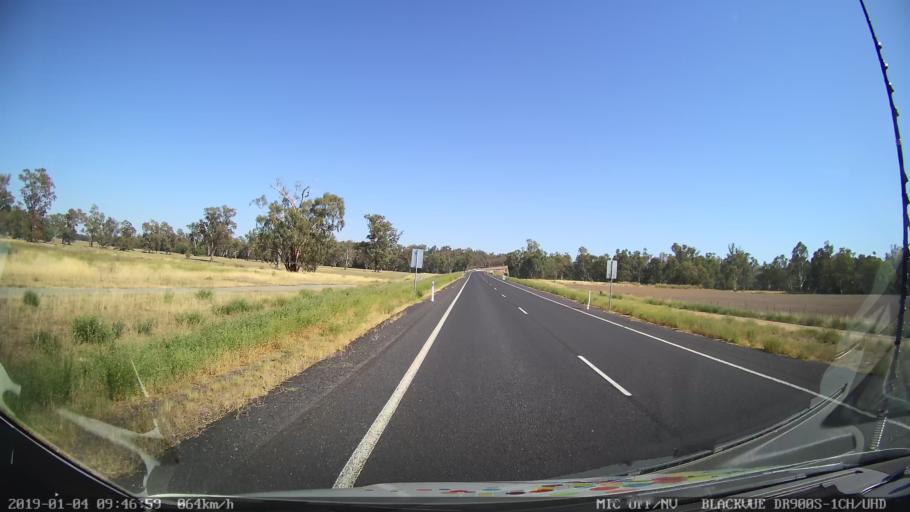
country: AU
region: New South Wales
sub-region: Cabonne
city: Canowindra
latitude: -33.6106
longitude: 148.4341
